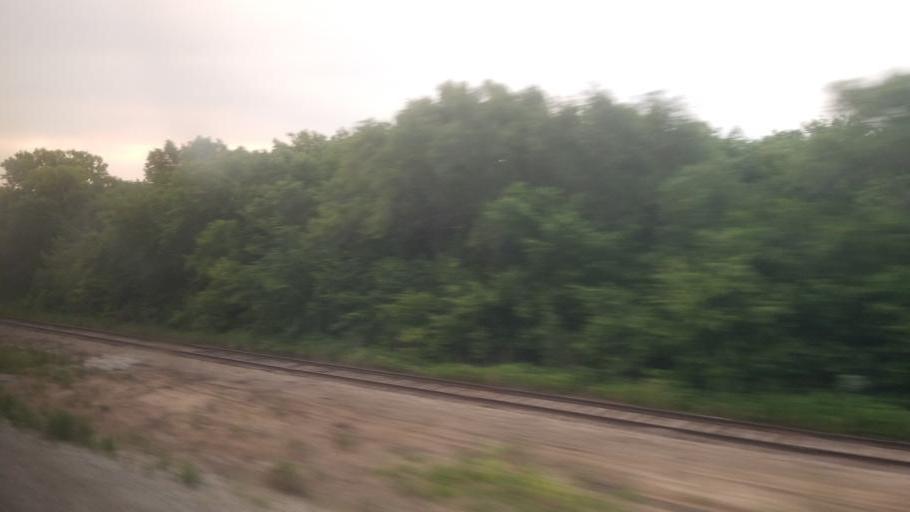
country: US
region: Kansas
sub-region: Marion County
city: Peabody
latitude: 38.1652
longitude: -97.1032
